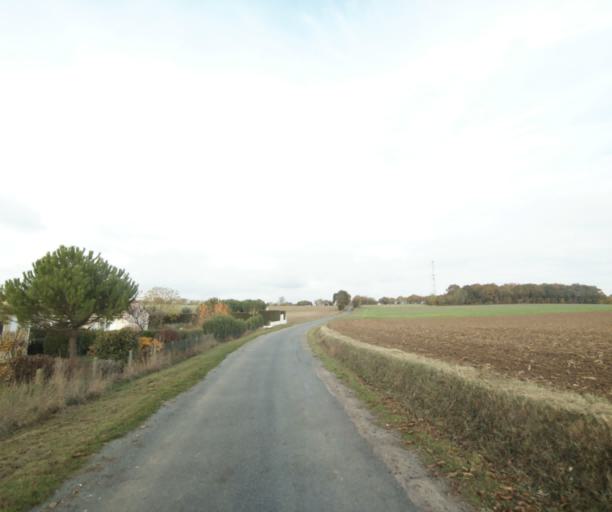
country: FR
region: Poitou-Charentes
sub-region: Departement de la Charente-Maritime
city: Saint-Georges-des-Coteaux
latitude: 45.7659
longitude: -0.7008
